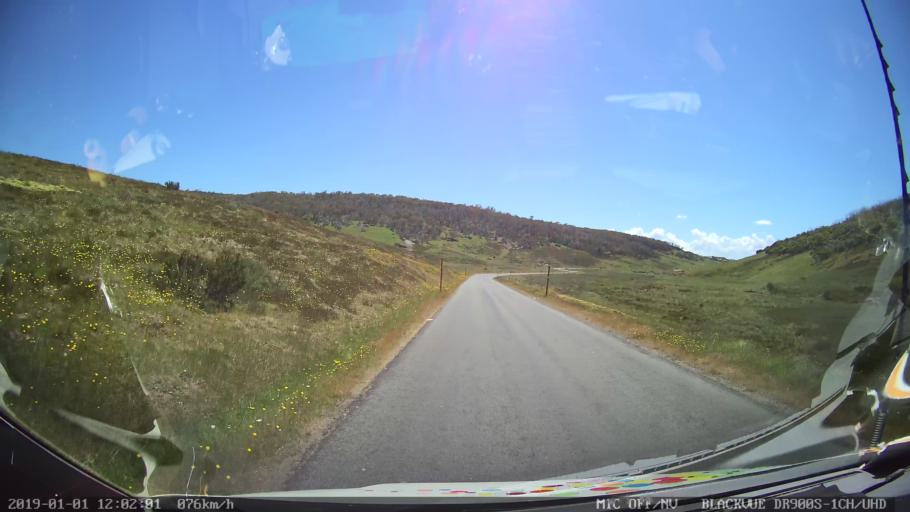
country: AU
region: New South Wales
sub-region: Snowy River
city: Jindabyne
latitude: -35.8756
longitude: 148.4734
